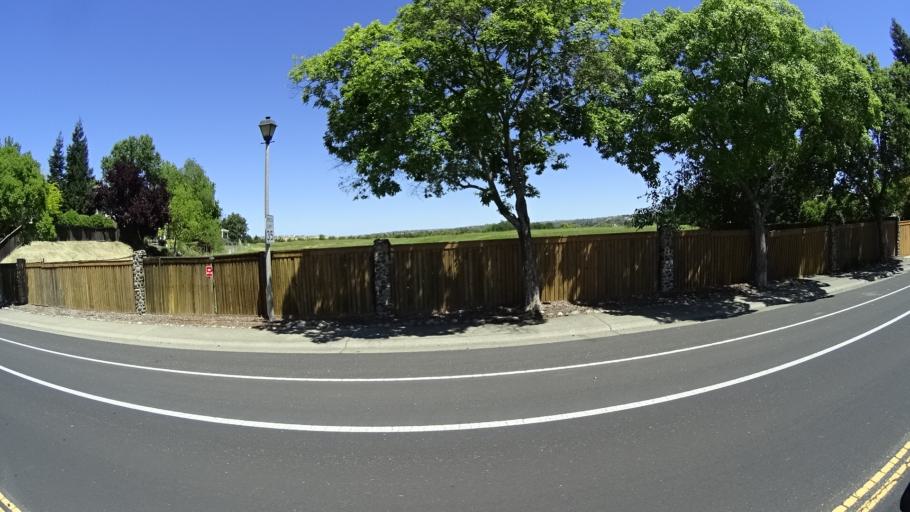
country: US
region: California
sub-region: Placer County
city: Rocklin
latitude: 38.8116
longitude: -121.2696
